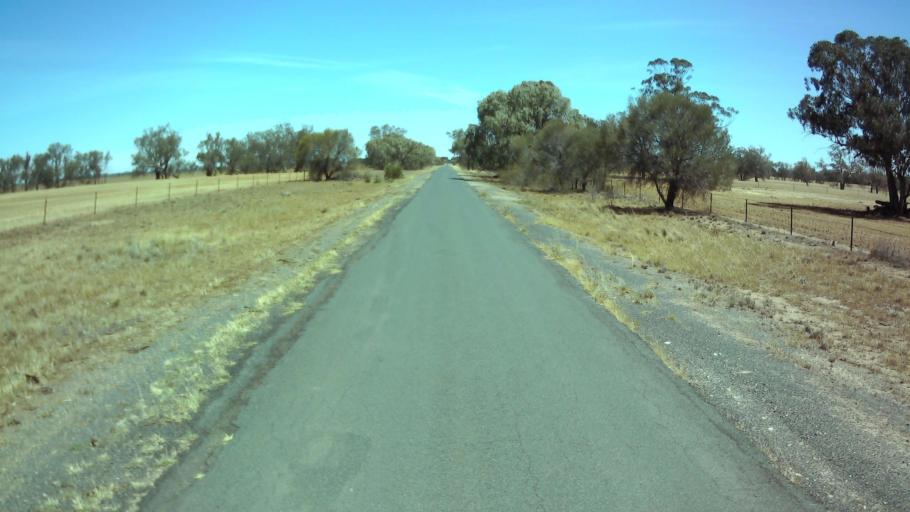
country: AU
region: New South Wales
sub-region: Weddin
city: Grenfell
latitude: -33.8471
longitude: 147.6963
